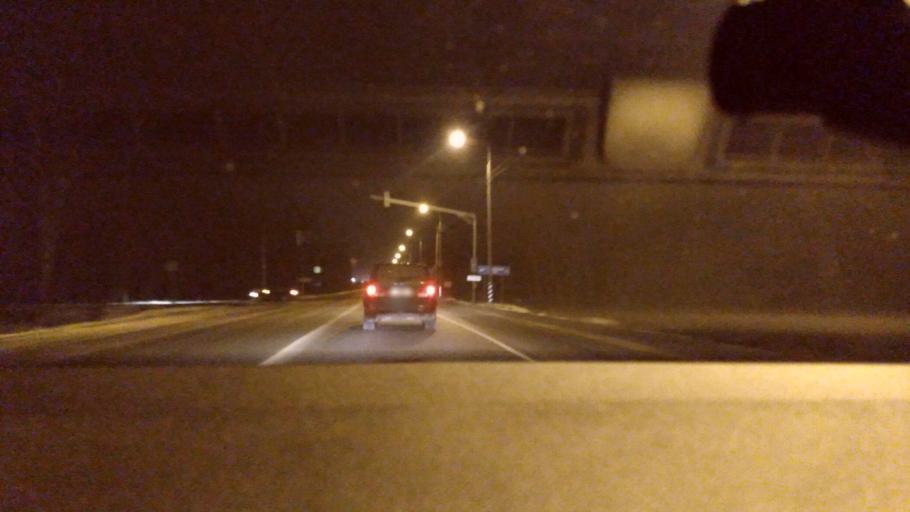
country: RU
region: Moskovskaya
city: Il'inskiy Pogost
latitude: 55.4882
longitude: 38.8949
